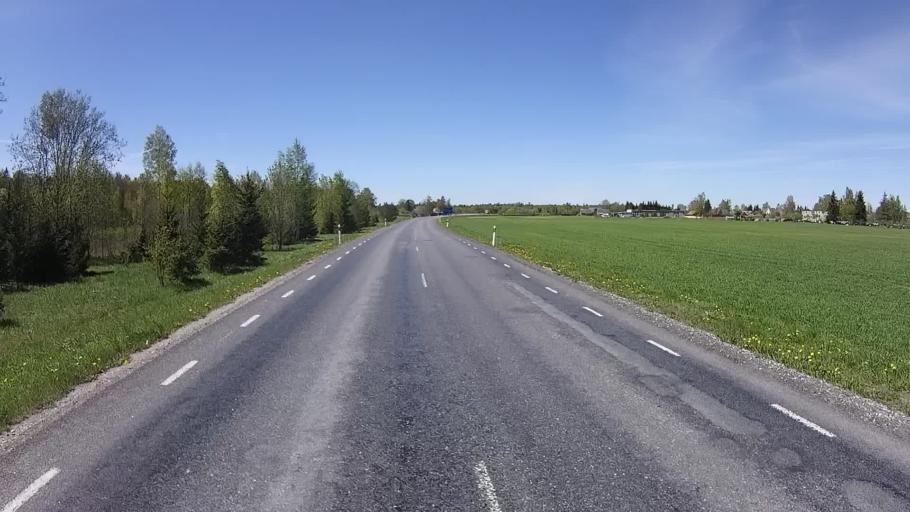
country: EE
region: Raplamaa
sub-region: Kehtna vald
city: Kehtna
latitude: 59.0544
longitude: 24.9584
